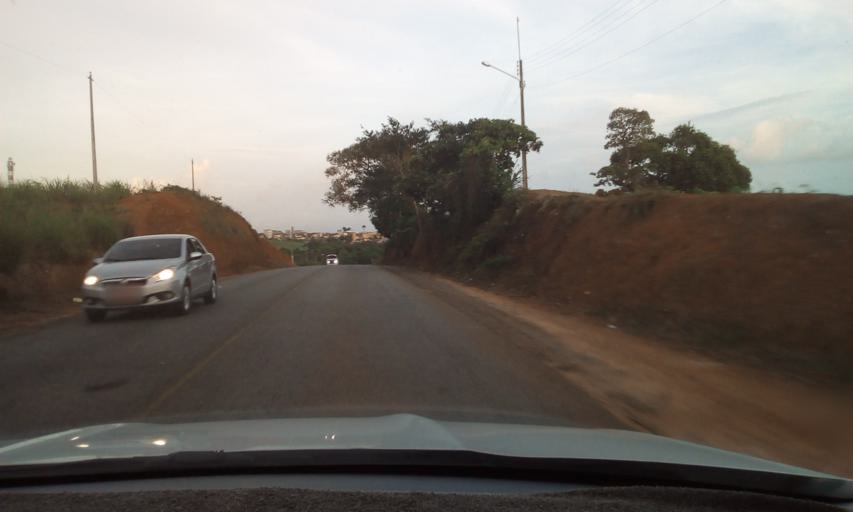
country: BR
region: Pernambuco
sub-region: Vicencia
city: Vicencia
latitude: -7.5998
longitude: -35.2401
